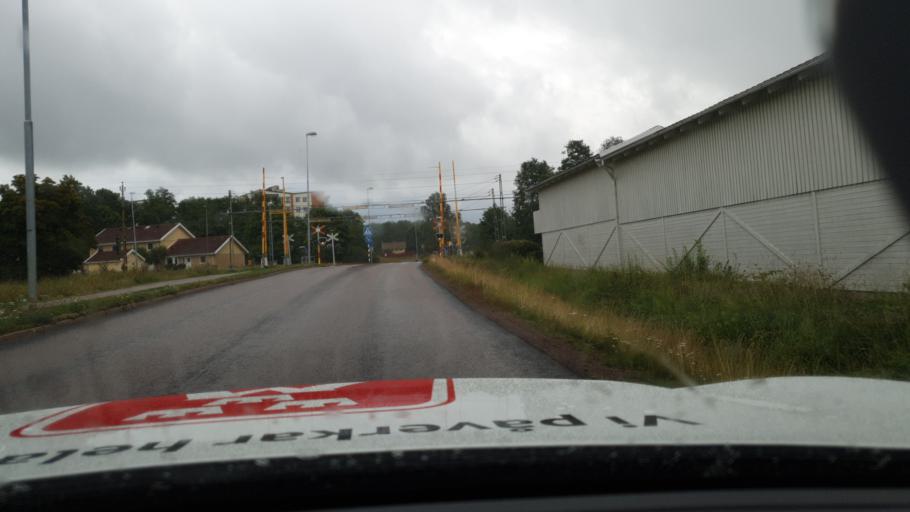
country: SE
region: Vaermland
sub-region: Kristinehamns Kommun
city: Kristinehamn
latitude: 59.3188
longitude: 14.1159
